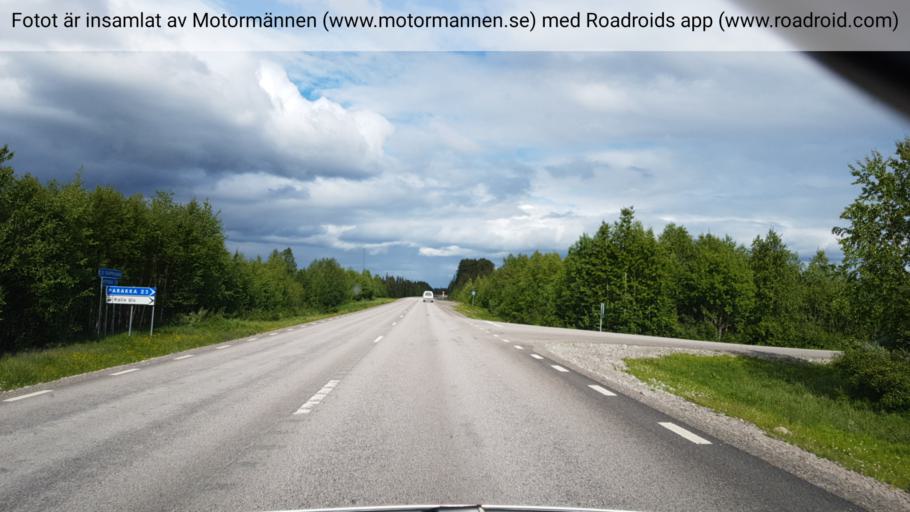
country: SE
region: Norrbotten
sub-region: Gallivare Kommun
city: Malmberget
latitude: 67.6630
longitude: 21.5801
